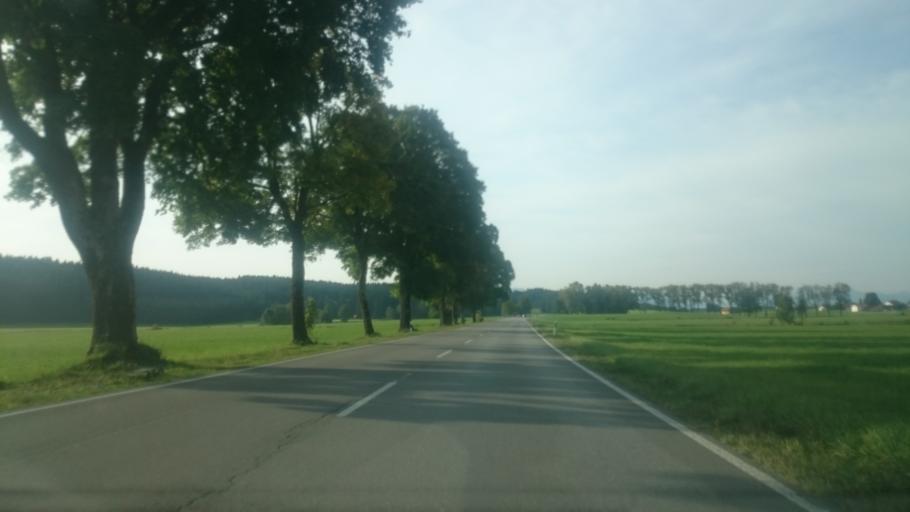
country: DE
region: Bavaria
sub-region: Upper Bavaria
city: Peiting
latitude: 47.7628
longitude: 10.9023
